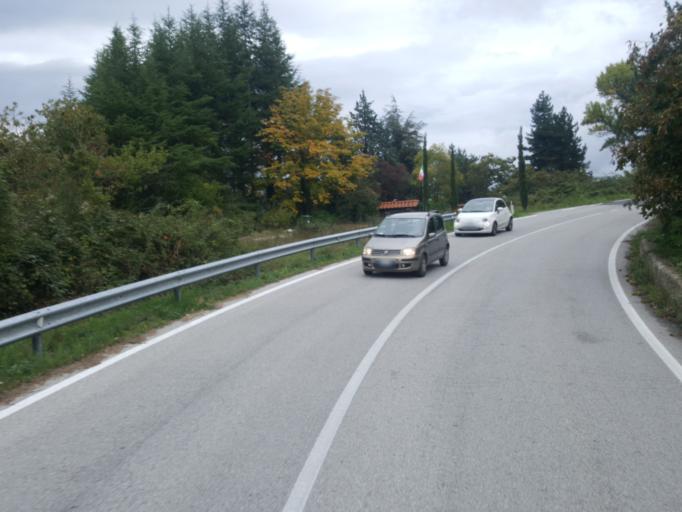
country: IT
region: Tuscany
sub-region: Province of Pisa
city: Castelnuovo di Val di Cecina
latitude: 43.2042
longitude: 10.9068
